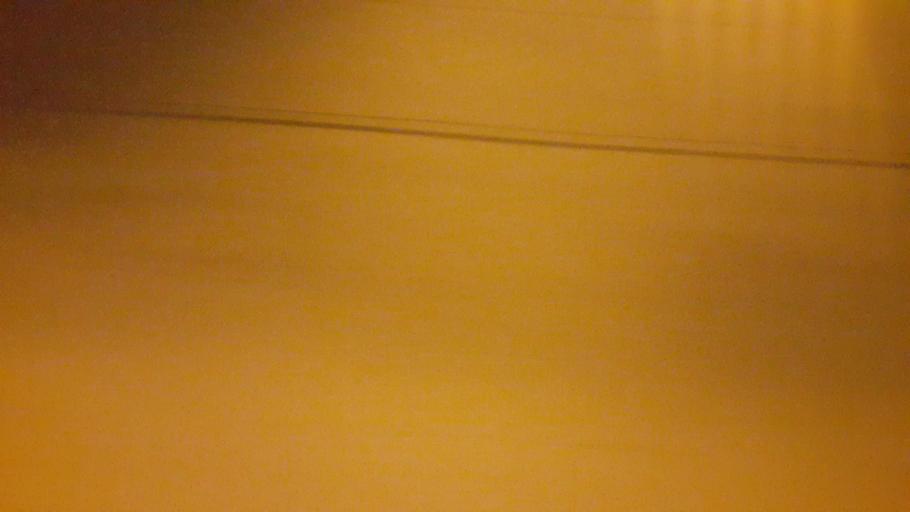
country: TR
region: Nigde
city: Ciftehan
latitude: 37.5117
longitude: 34.8185
